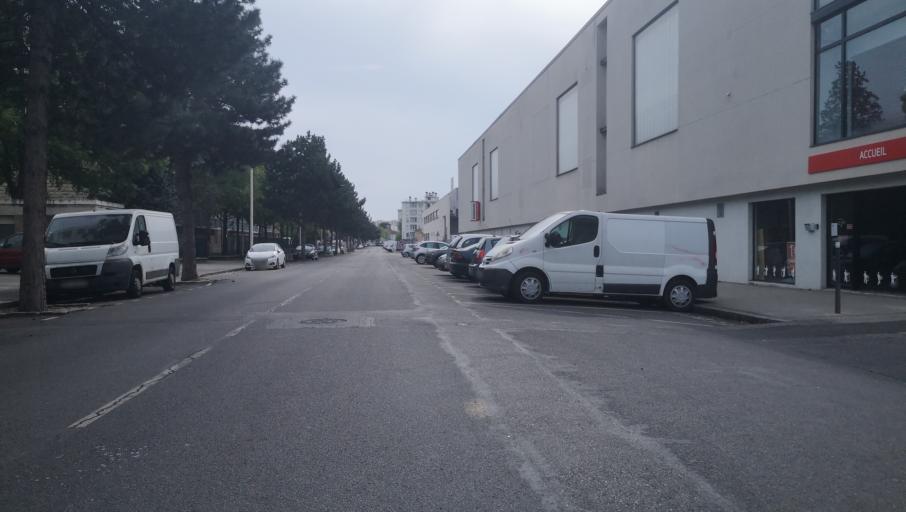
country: FR
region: Rhone-Alpes
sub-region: Departement du Rhone
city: Saint-Fons
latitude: 45.7341
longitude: 4.8704
